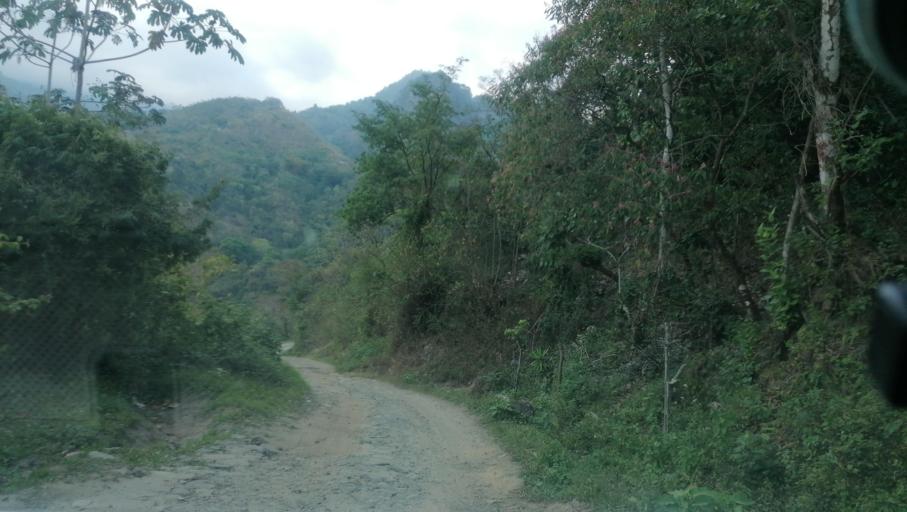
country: MX
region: Chiapas
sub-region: Cacahoatan
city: Benito Juarez
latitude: 15.1410
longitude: -92.1908
